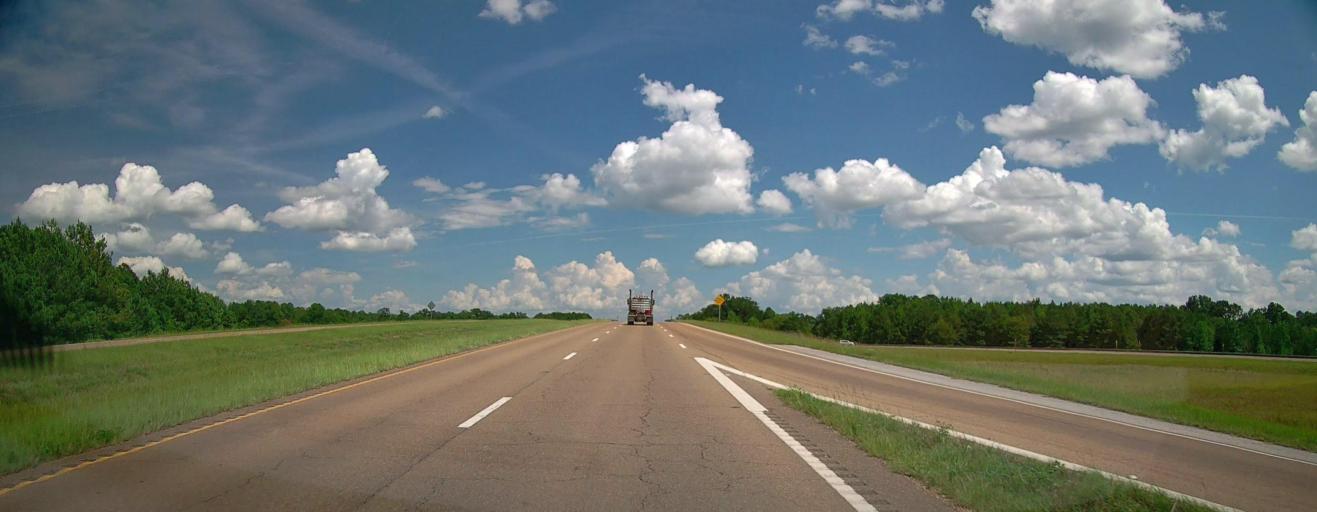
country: US
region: Mississippi
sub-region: Monroe County
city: Aberdeen
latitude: 33.8144
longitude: -88.4932
